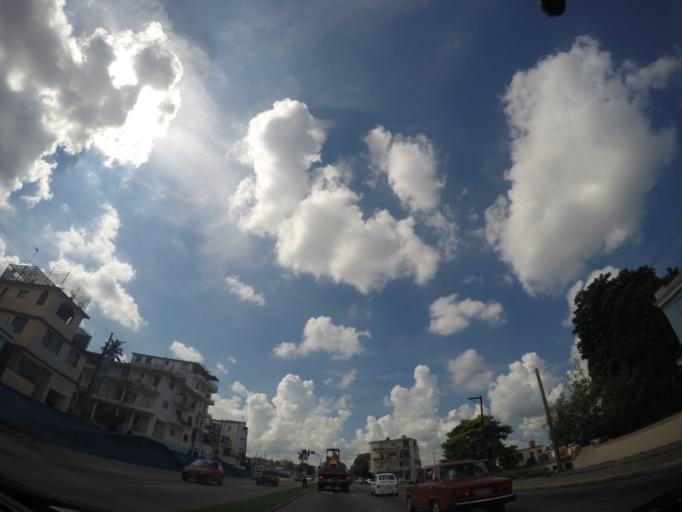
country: CU
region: La Habana
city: Cerro
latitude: 23.1027
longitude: -82.4201
